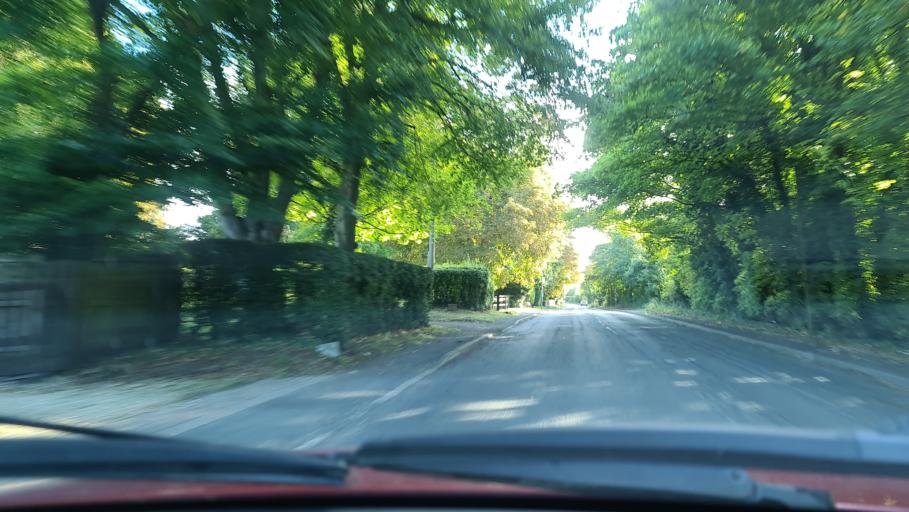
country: GB
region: England
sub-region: Oxfordshire
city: Chinnor
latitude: 51.6807
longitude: -0.9505
